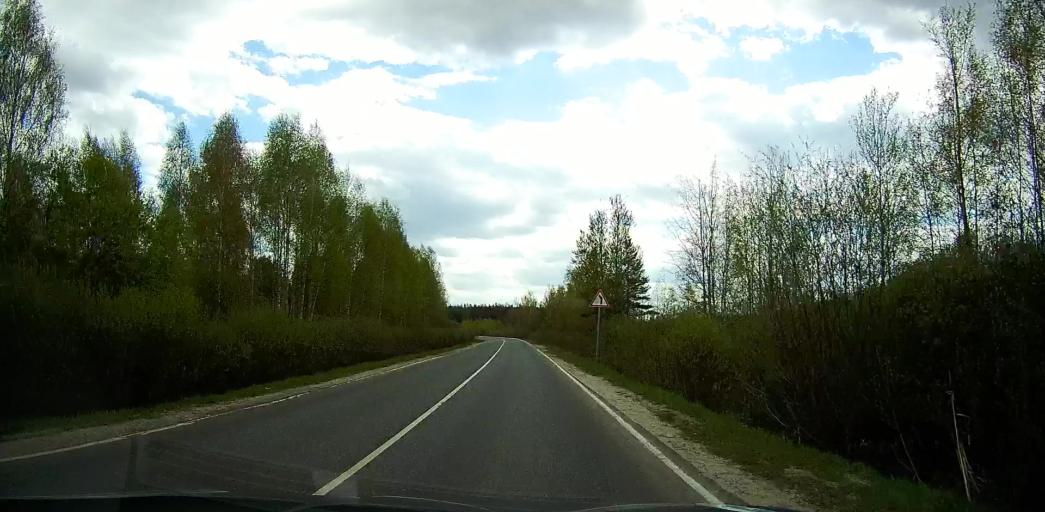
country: RU
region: Moskovskaya
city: Davydovo
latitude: 55.6606
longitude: 38.7546
